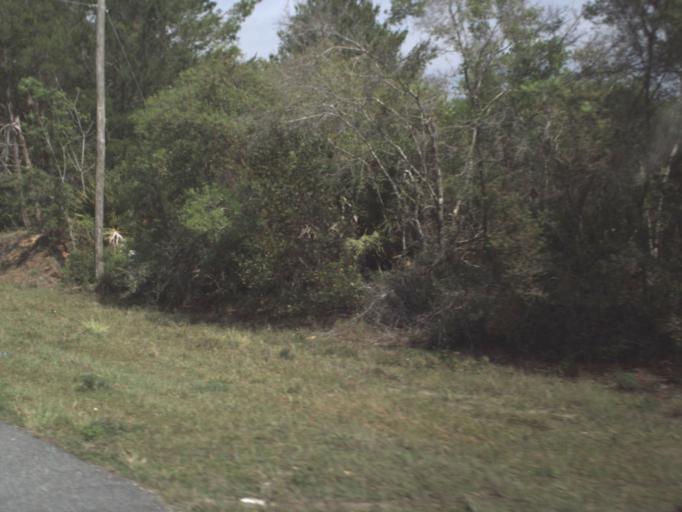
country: US
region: Florida
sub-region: Lake County
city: Astor
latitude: 29.1565
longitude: -81.5801
